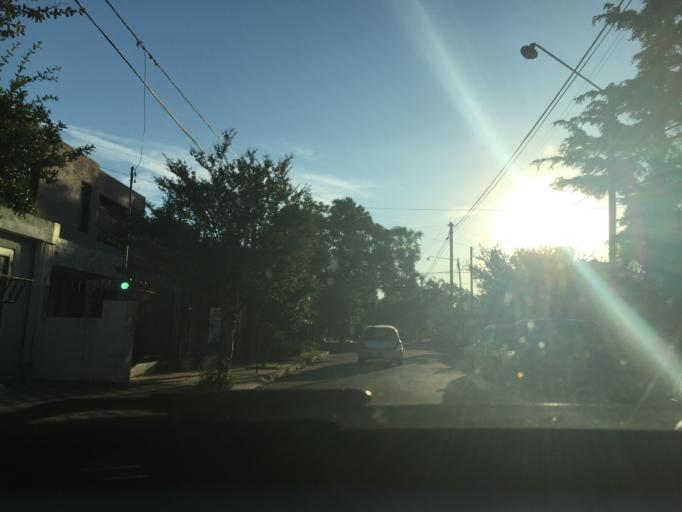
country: AR
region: Cordoba
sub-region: Departamento de Capital
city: Cordoba
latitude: -31.3626
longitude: -64.2290
